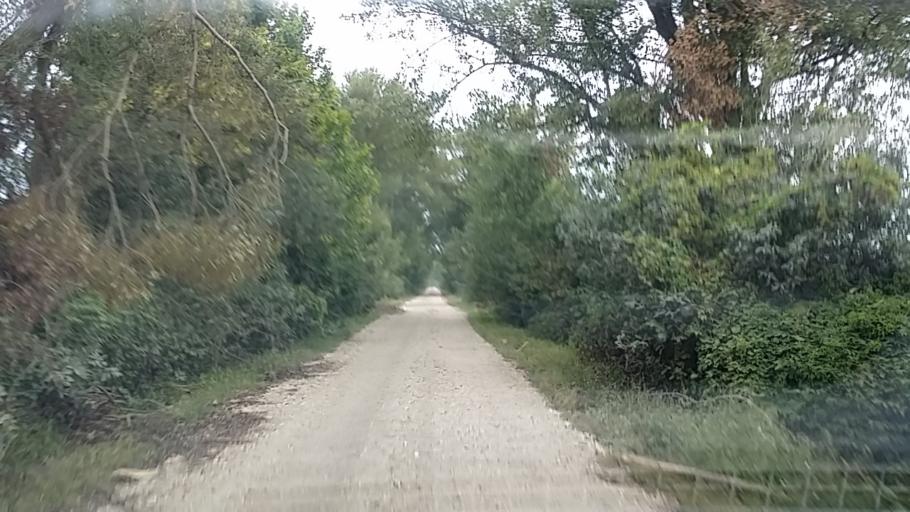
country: HU
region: Gyor-Moson-Sopron
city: Farad
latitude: 47.6635
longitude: 17.1383
